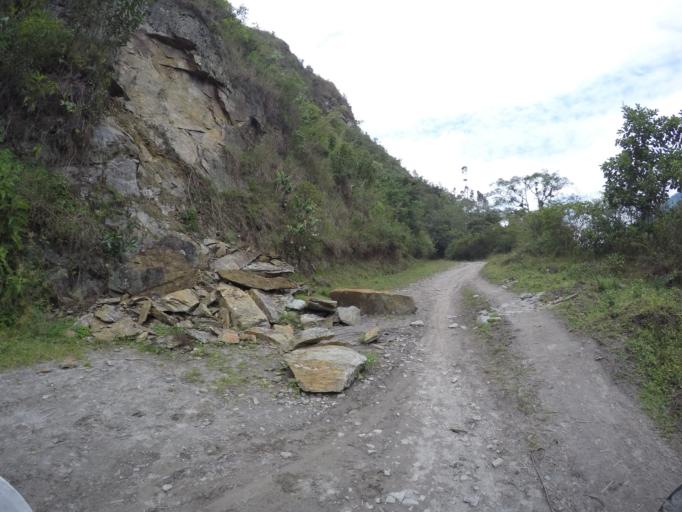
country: CO
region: Tolima
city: Cajamarca
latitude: 4.5330
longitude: -75.4104
